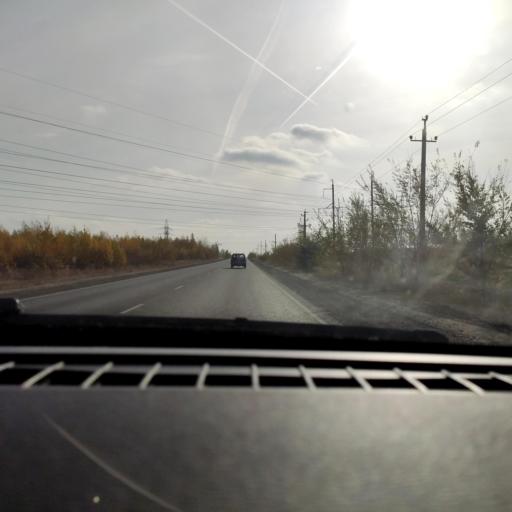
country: RU
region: Voronezj
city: Maslovka
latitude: 51.5832
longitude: 39.2592
